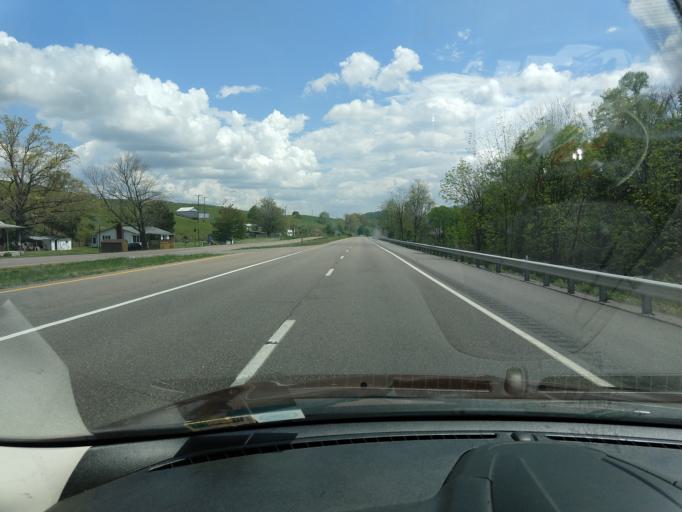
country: US
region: Virginia
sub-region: Russell County
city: Honaker
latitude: 36.9780
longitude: -81.8722
